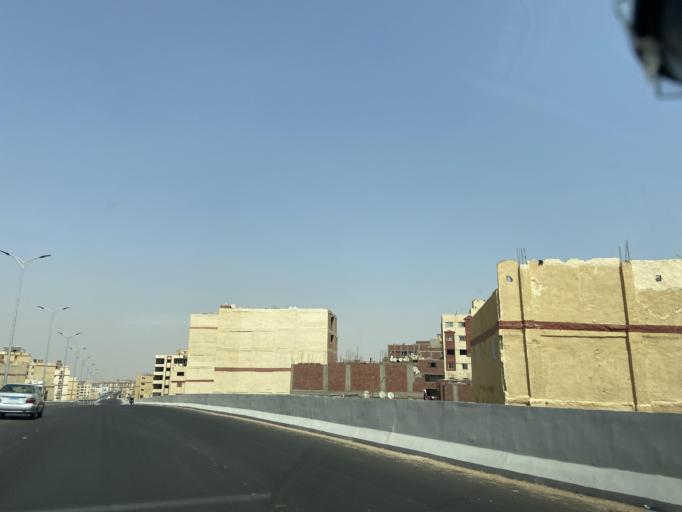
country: EG
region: Muhafazat al Qahirah
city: Cairo
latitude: 30.0634
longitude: 31.3806
